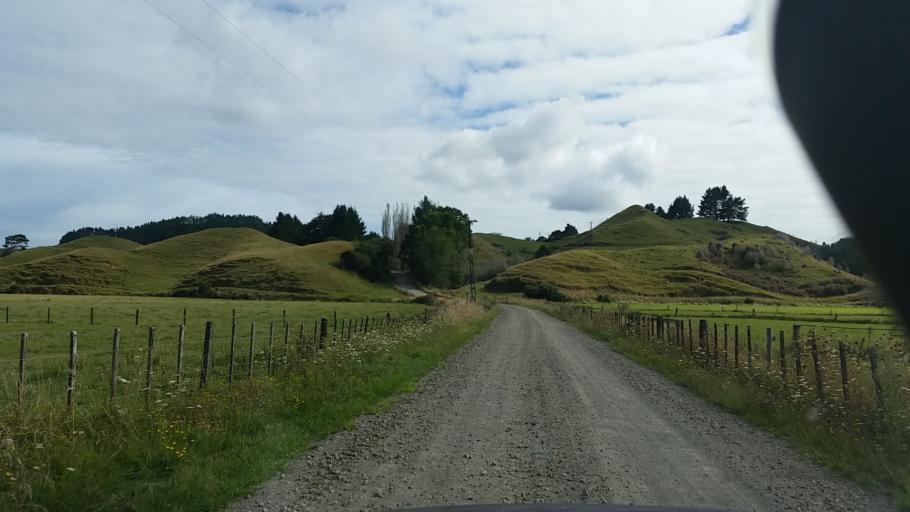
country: NZ
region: Taranaki
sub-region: South Taranaki District
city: Eltham
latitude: -39.2481
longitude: 174.4694
